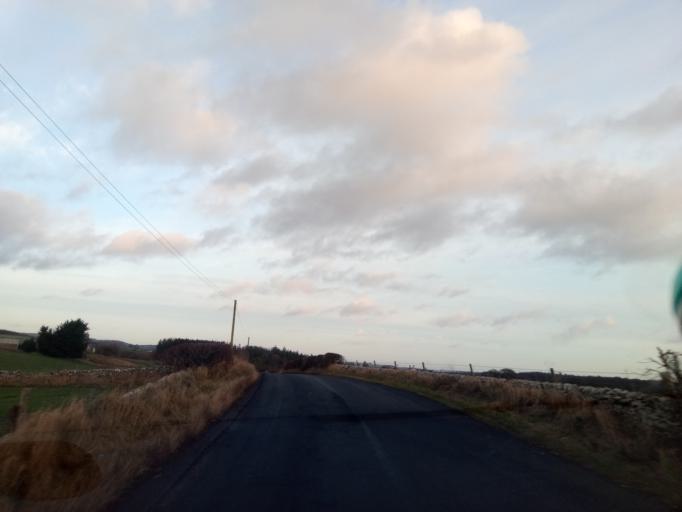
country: GB
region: Scotland
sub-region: The Scottish Borders
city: Newtown St Boswells
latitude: 55.5474
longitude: -2.7013
